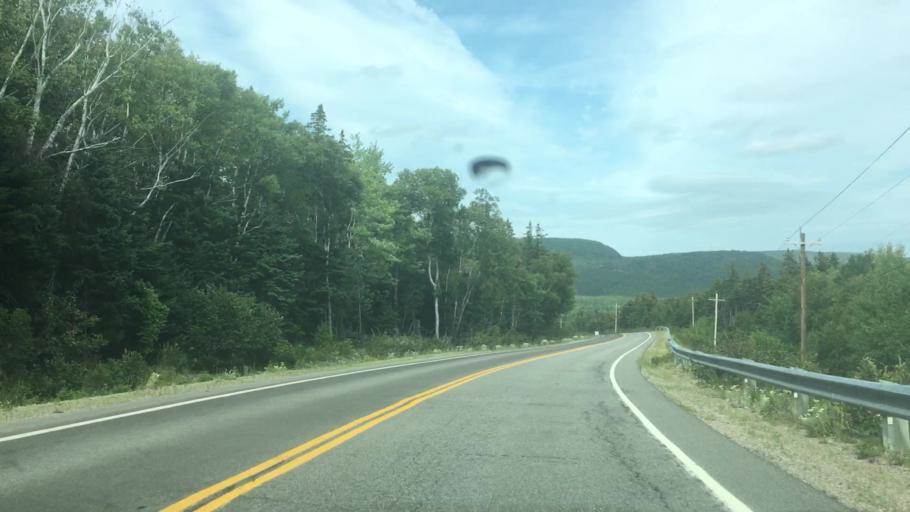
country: CA
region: Nova Scotia
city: Sydney Mines
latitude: 46.5394
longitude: -60.4142
